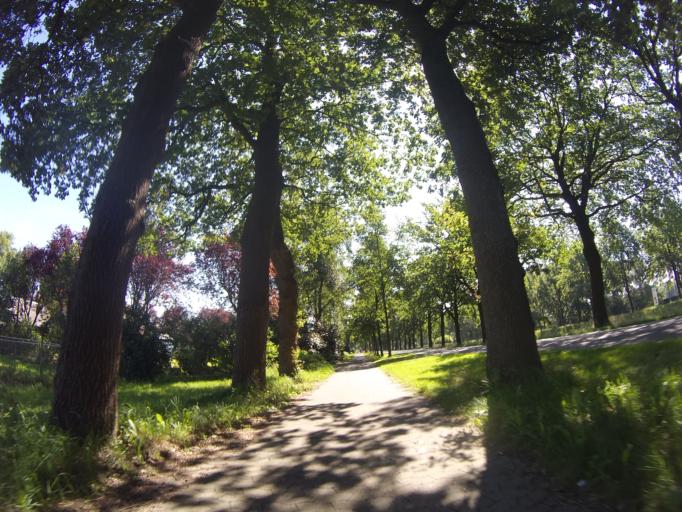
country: NL
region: Drenthe
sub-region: Gemeente Emmen
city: Schoonebeek
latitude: 52.7118
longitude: 6.9049
